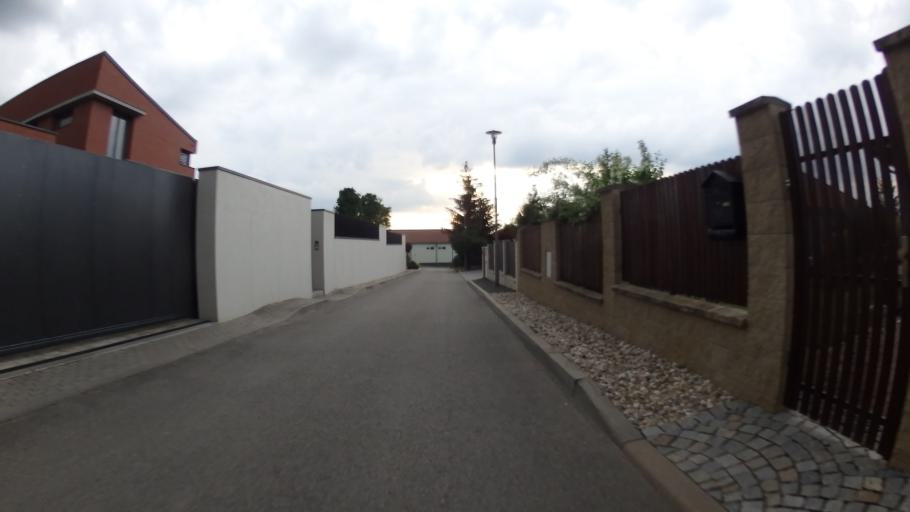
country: CZ
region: South Moravian
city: Ostopovice
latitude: 49.1400
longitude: 16.5522
